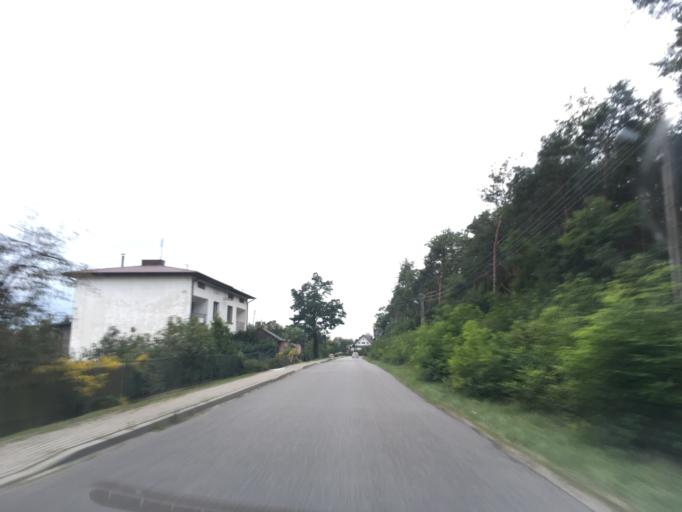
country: PL
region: Lodz Voivodeship
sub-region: Powiat piotrkowski
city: Reczno
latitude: 51.1900
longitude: 19.8406
